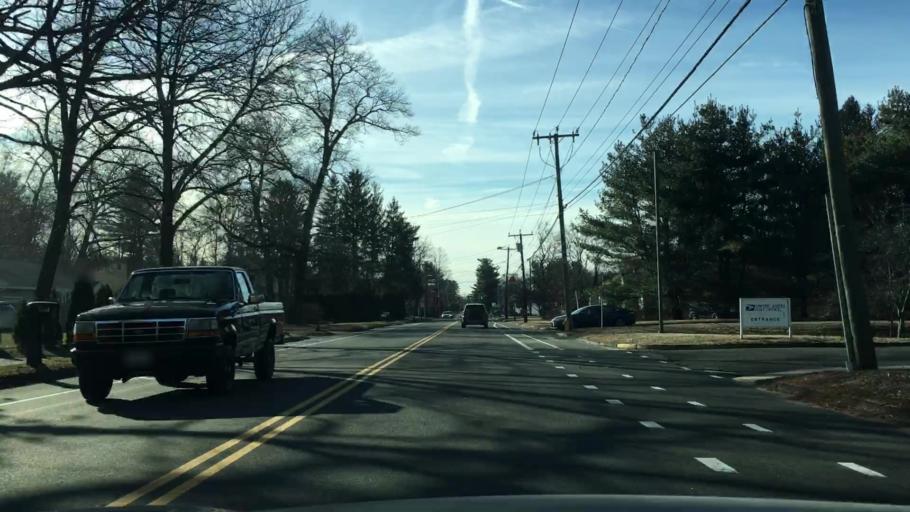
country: US
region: Massachusetts
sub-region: Hampden County
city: Agawam
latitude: 42.0694
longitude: -72.6313
